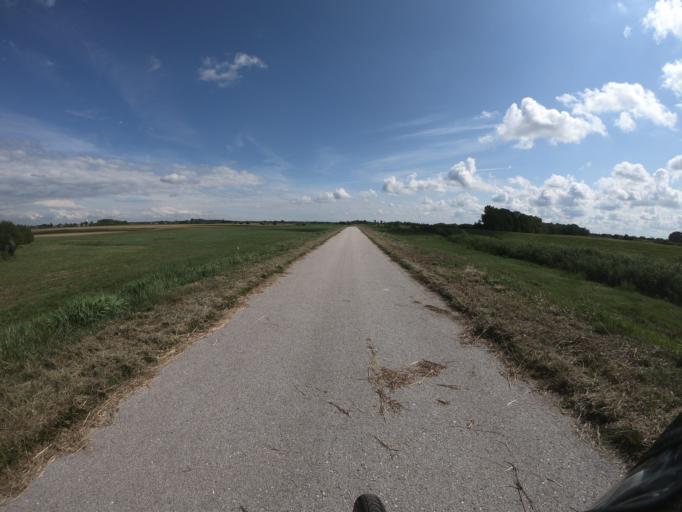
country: HU
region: Heves
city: Poroszlo
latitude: 47.7062
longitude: 20.6851
